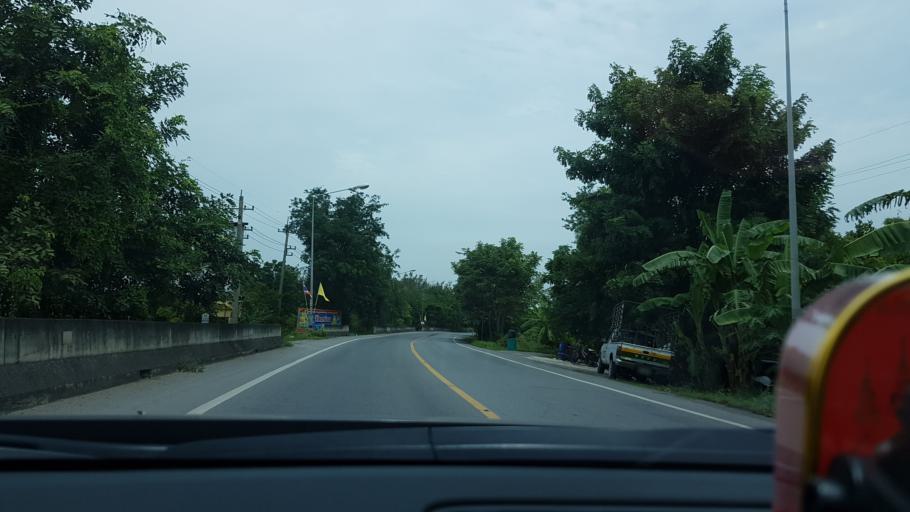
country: TH
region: Pathum Thani
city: Sam Khok
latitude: 14.1218
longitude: 100.5526
